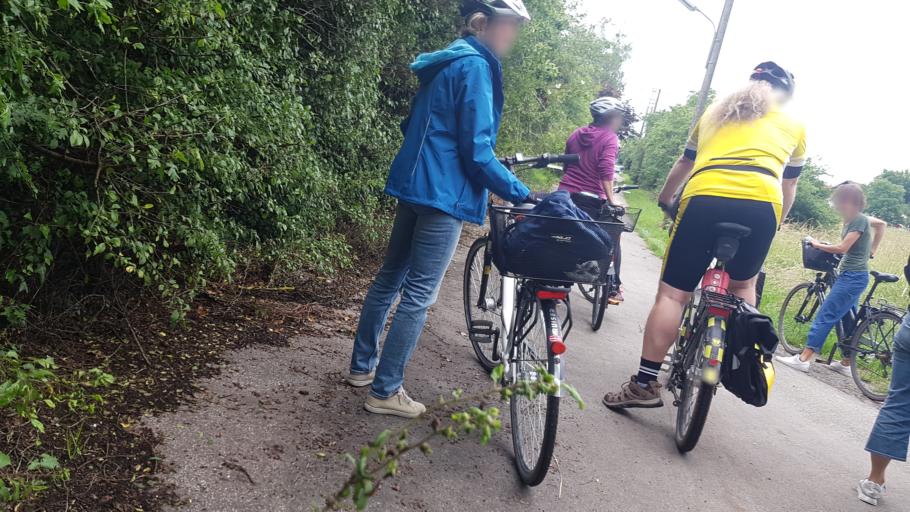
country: DE
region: Bavaria
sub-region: Upper Bavaria
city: Pasing
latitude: 48.1503
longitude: 11.4285
